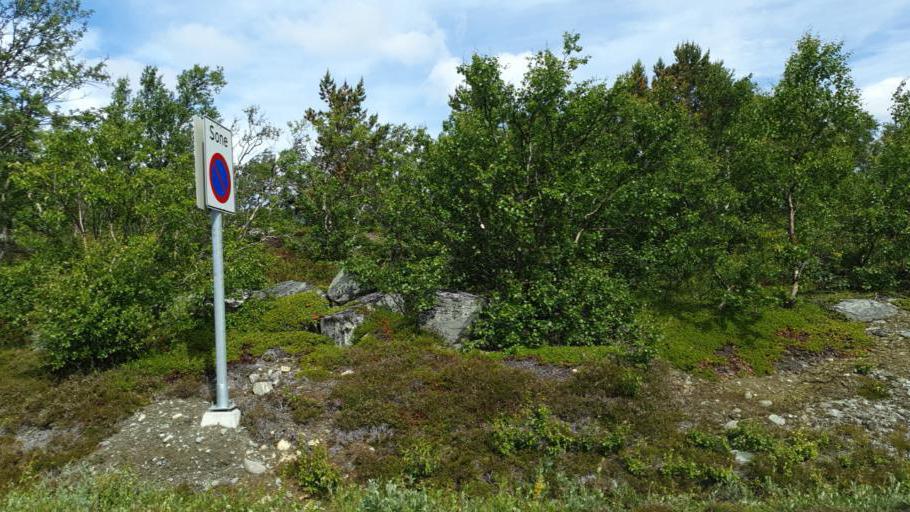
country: NO
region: Oppland
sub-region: Oystre Slidre
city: Heggenes
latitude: 61.4894
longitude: 8.8390
